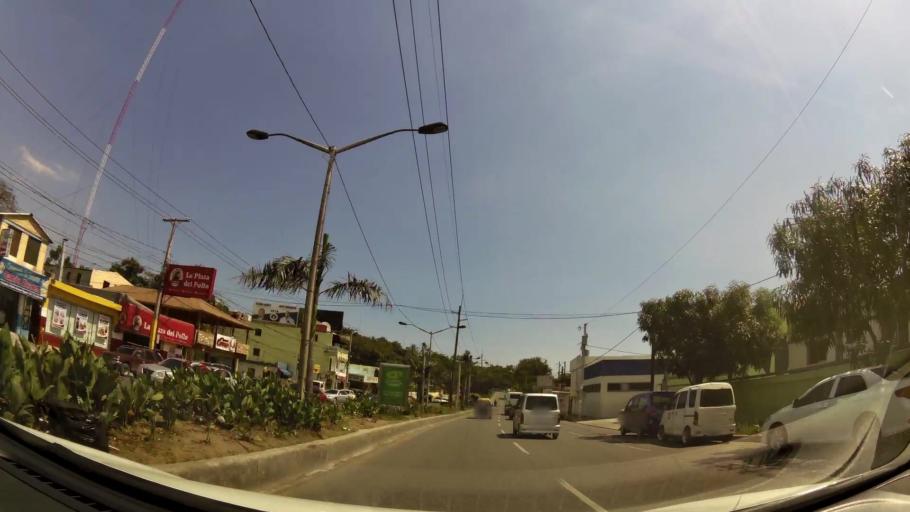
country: DO
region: Santo Domingo
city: Santo Domingo Oeste
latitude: 18.4767
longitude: -69.9959
